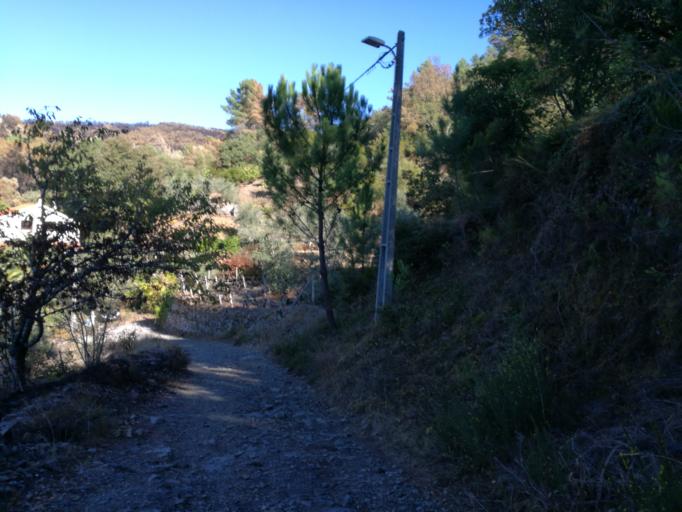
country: PT
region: Leiria
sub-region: Pedrogao Grande
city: Pedrogao Grande
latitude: 39.9154
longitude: -8.0633
